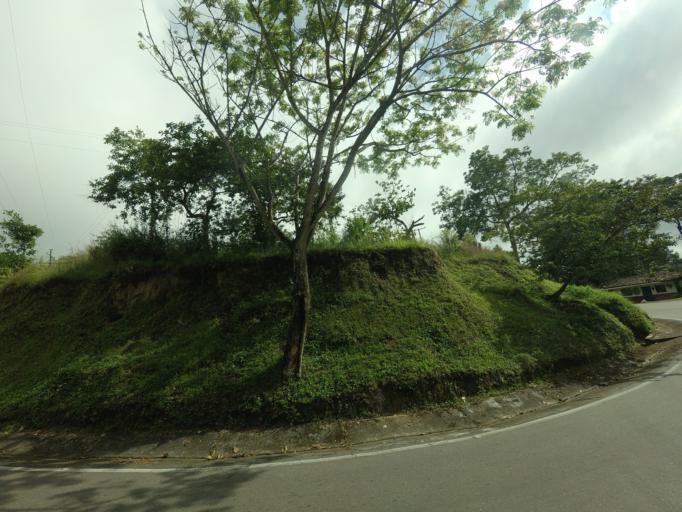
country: CO
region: Huila
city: San Agustin
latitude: 1.8870
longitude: -76.2874
